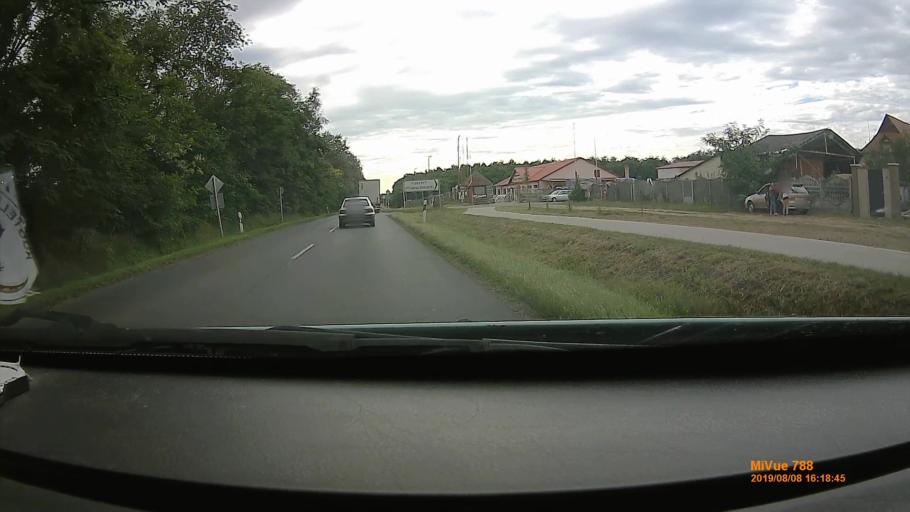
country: HU
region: Szabolcs-Szatmar-Bereg
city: Mateszalka
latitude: 47.9650
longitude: 22.2824
